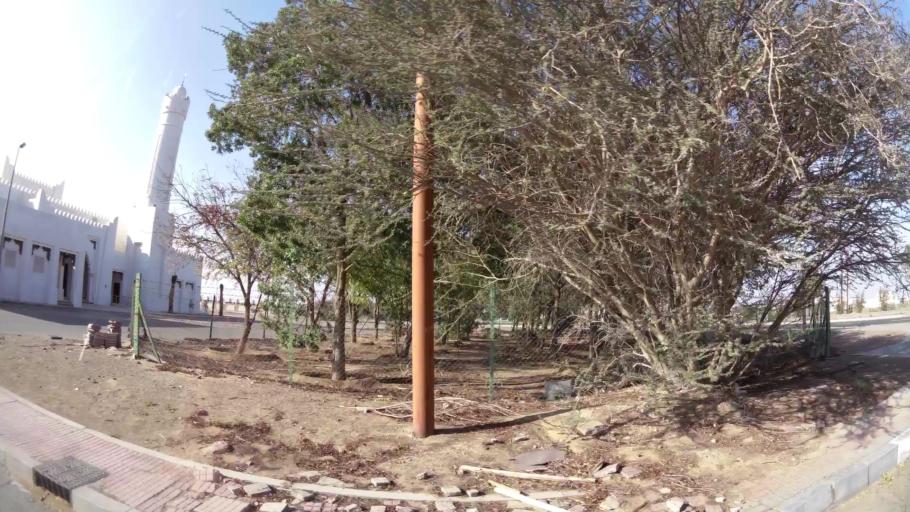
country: AE
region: Abu Dhabi
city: Al Ain
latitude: 24.0438
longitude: 55.8424
